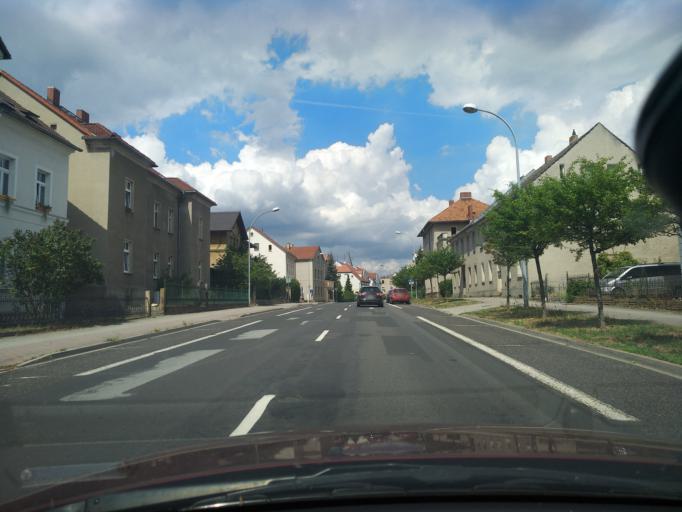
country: DE
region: Saxony
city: Niesky
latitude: 51.2892
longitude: 14.8208
